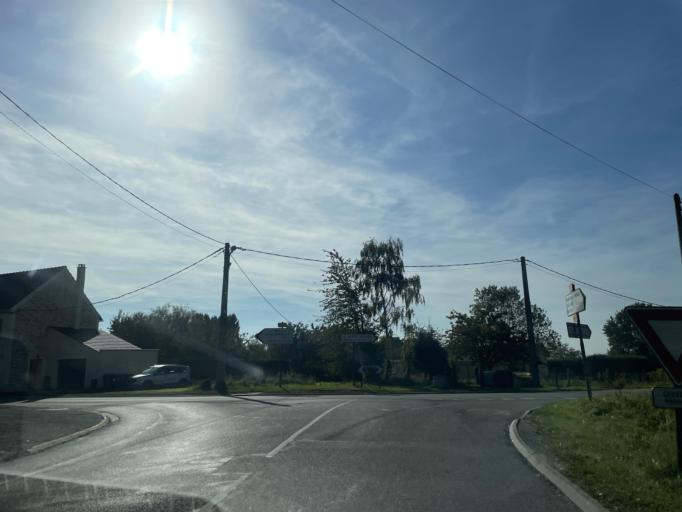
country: FR
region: Ile-de-France
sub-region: Departement de Seine-et-Marne
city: Saint-Jean-les-Deux-Jumeaux
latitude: 48.9003
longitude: 3.0355
